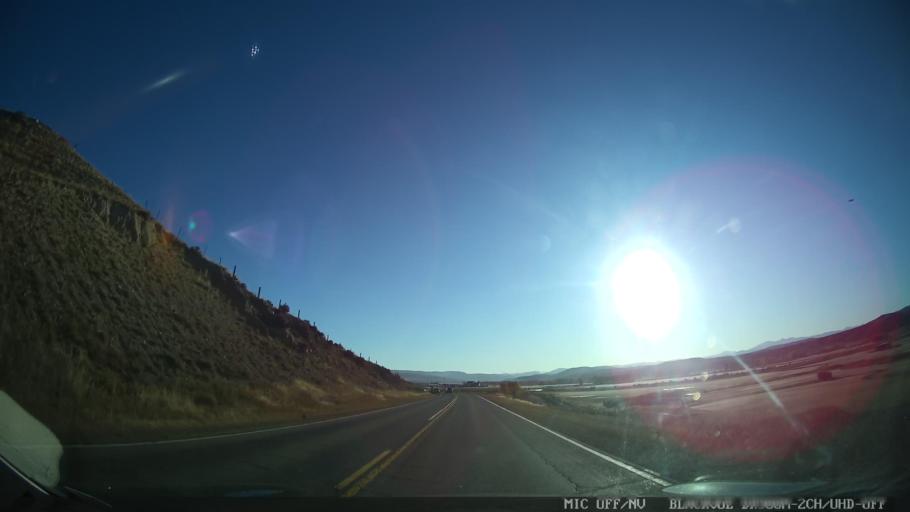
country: US
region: Colorado
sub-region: Grand County
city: Kremmling
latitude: 40.0530
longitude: -106.3370
